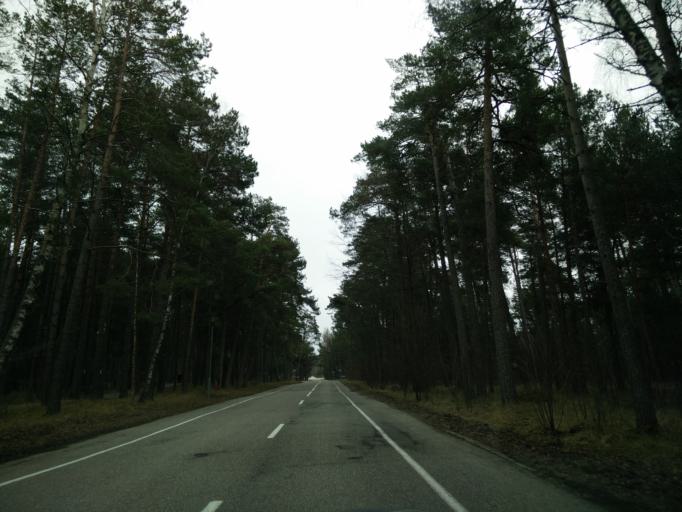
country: LT
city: Nida
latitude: 55.3014
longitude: 20.9824
